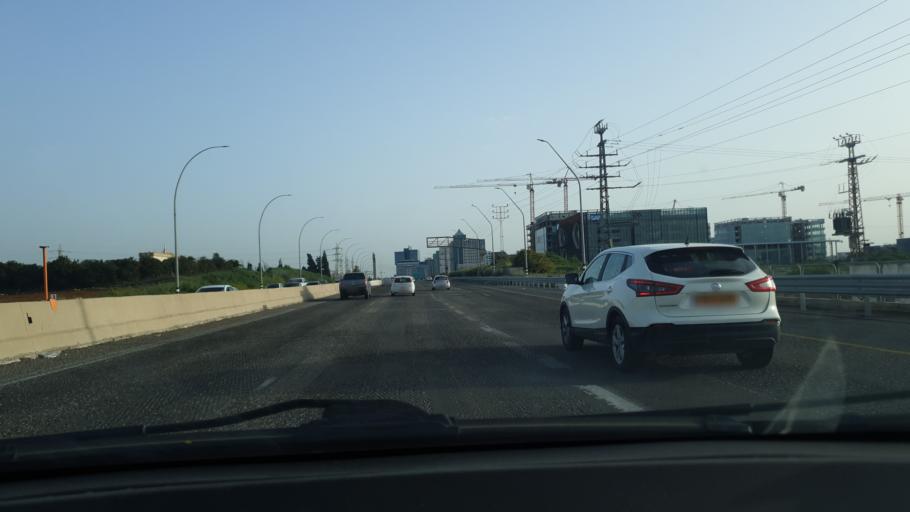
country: IL
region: Central District
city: Ra'anana
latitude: 32.2048
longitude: 34.8842
